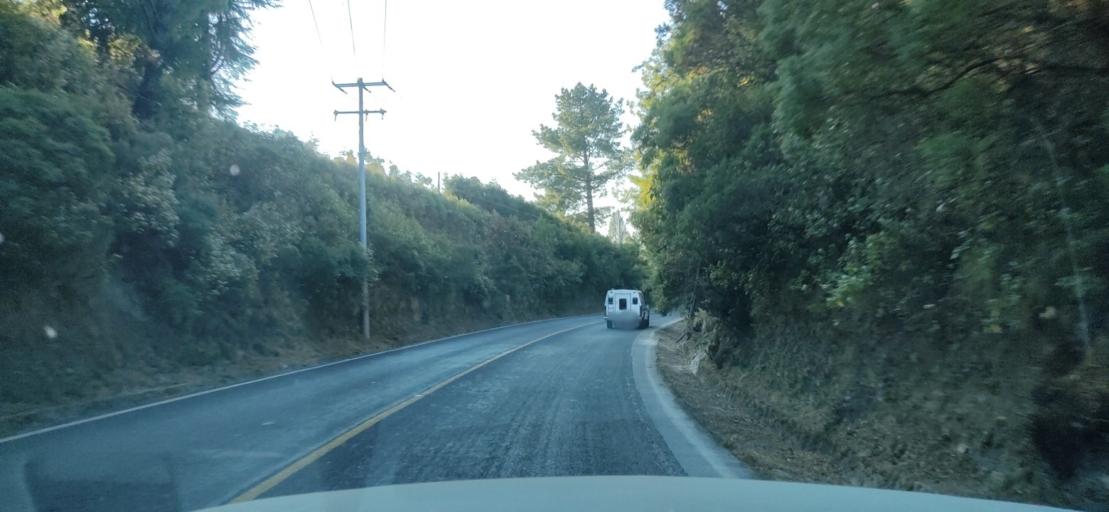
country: MX
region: Mexico
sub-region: Ocoyoacac
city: San Jeronimo Acazulco
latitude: 19.2528
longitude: -99.3771
